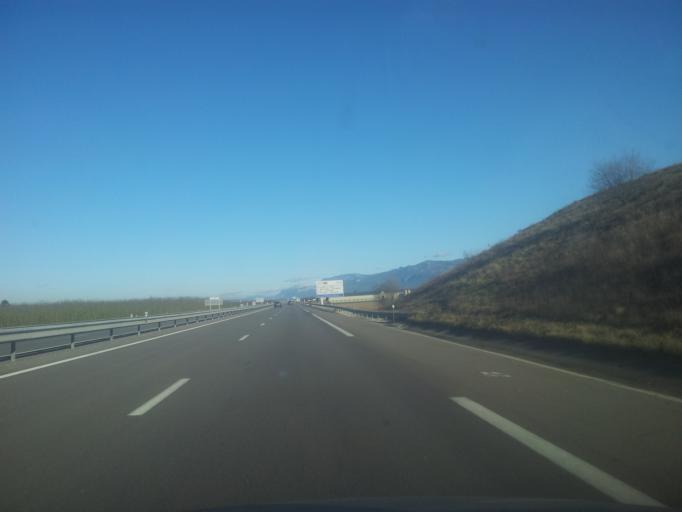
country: FR
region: Rhone-Alpes
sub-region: Departement de l'Isere
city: Saint-Lattier
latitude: 45.0570
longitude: 5.1883
